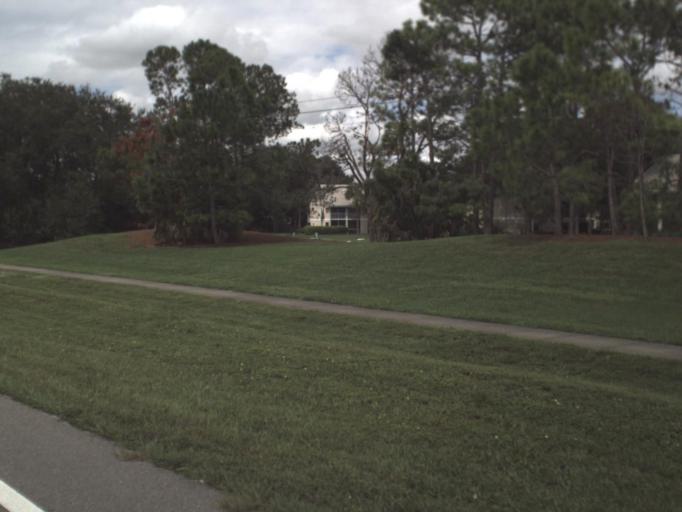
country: US
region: Florida
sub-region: Sarasota County
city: Desoto Lakes
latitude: 27.3885
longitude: -82.4914
